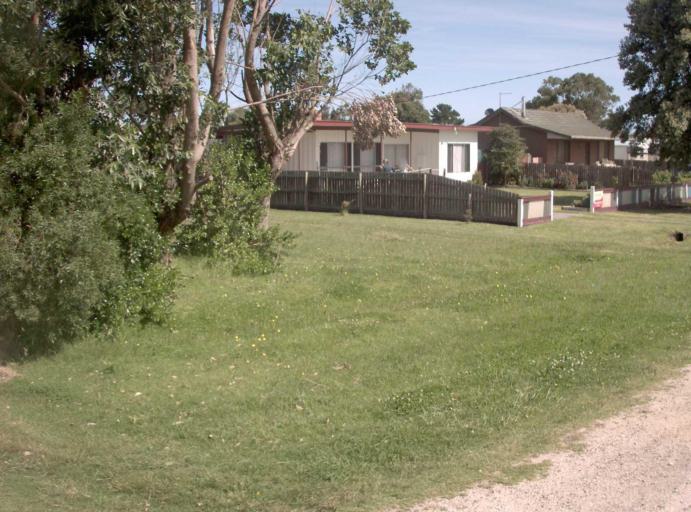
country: AU
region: Victoria
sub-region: Wellington
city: Sale
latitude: -38.3715
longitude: 147.1888
